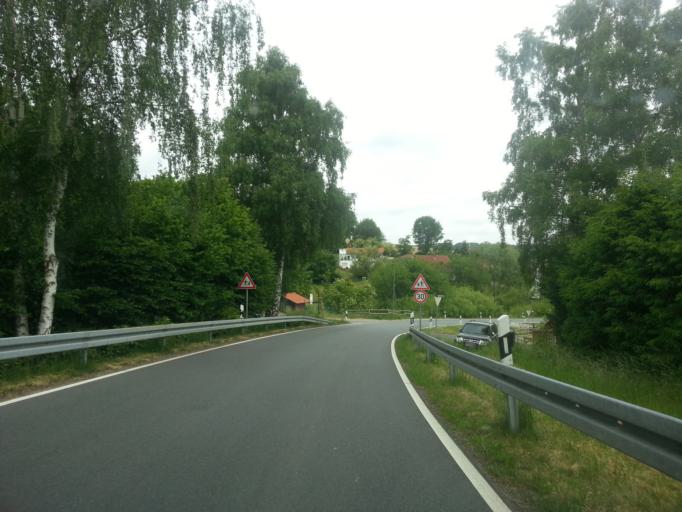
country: DE
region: Hesse
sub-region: Regierungsbezirk Darmstadt
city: Seeheim-Jugenheim
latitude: 49.7419
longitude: 8.6960
